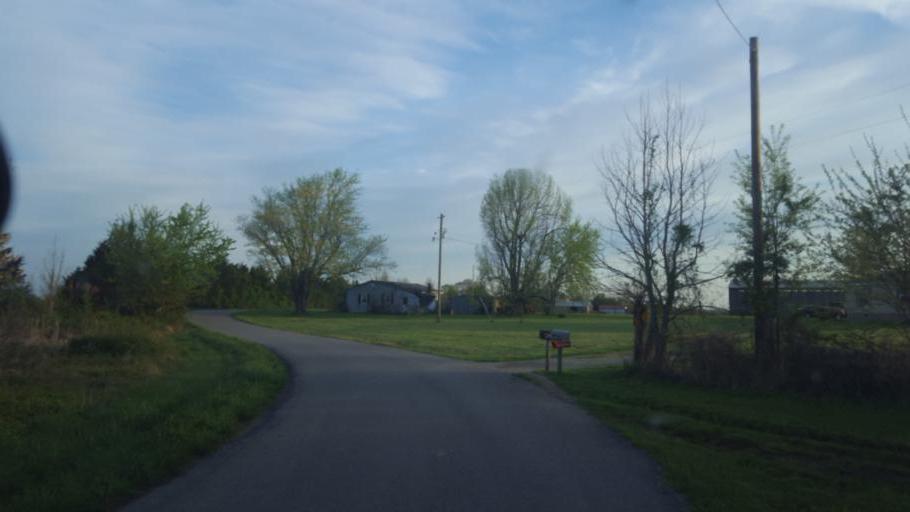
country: US
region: Kentucky
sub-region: Barren County
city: Cave City
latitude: 37.1590
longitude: -86.0118
